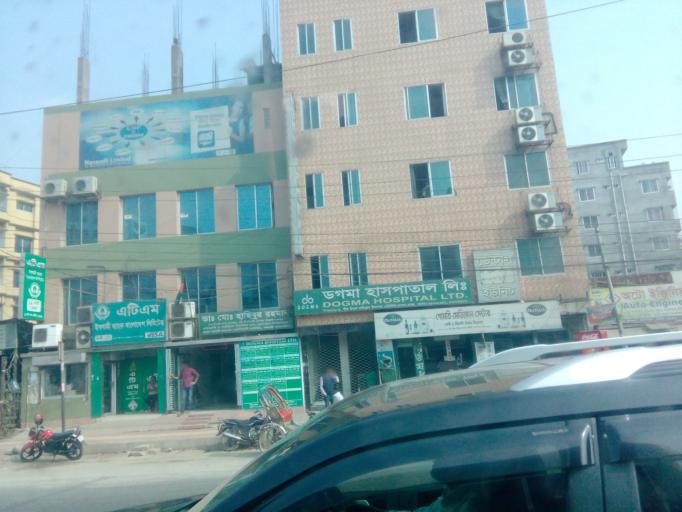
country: BD
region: Dhaka
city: Paltan
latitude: 23.7874
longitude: 90.4255
